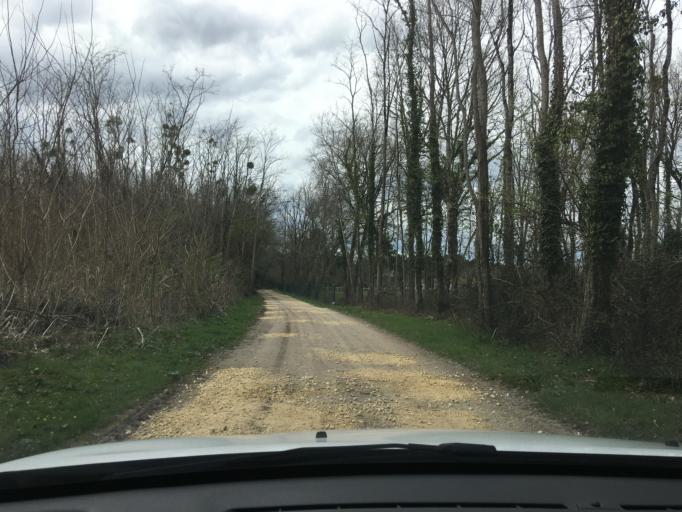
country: FR
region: Aquitaine
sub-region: Departement de la Gironde
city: Saint-Sauveur
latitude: 45.2226
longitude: -0.8682
